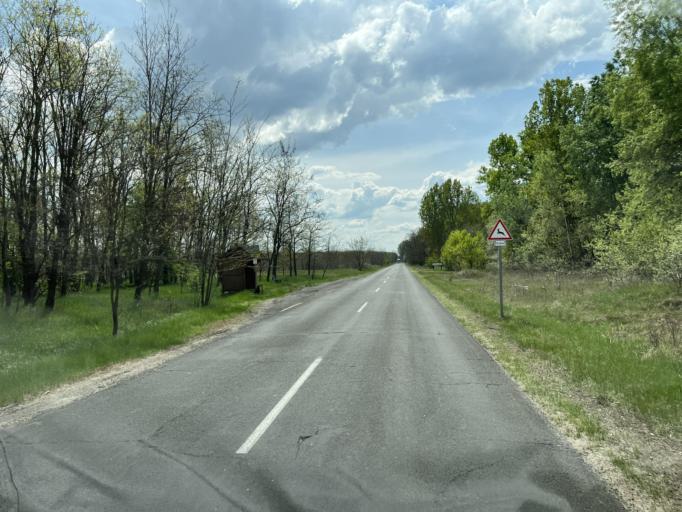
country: HU
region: Pest
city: Csemo
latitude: 47.1124
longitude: 19.6463
